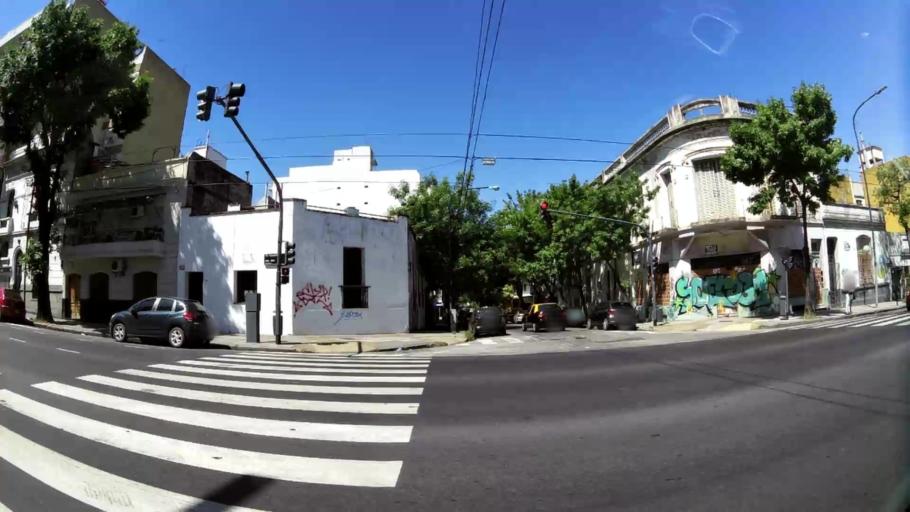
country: AR
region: Buenos Aires F.D.
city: Villa Santa Rita
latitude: -34.6336
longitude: -58.4535
